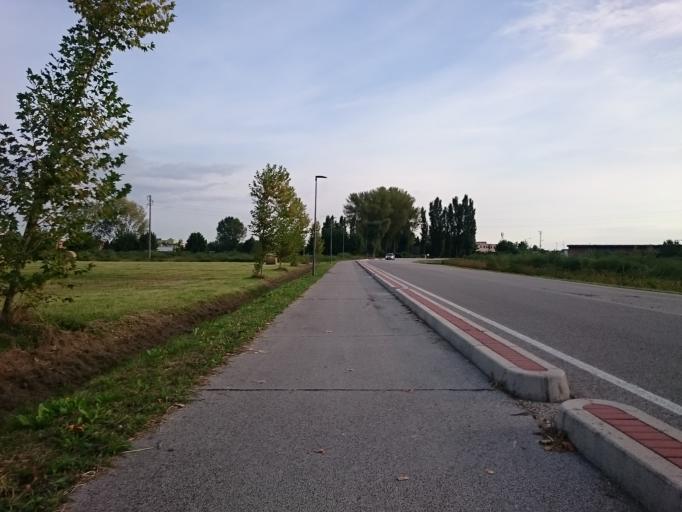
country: IT
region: Veneto
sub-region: Provincia di Vicenza
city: Camisano Vicentino
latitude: 45.5211
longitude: 11.7008
